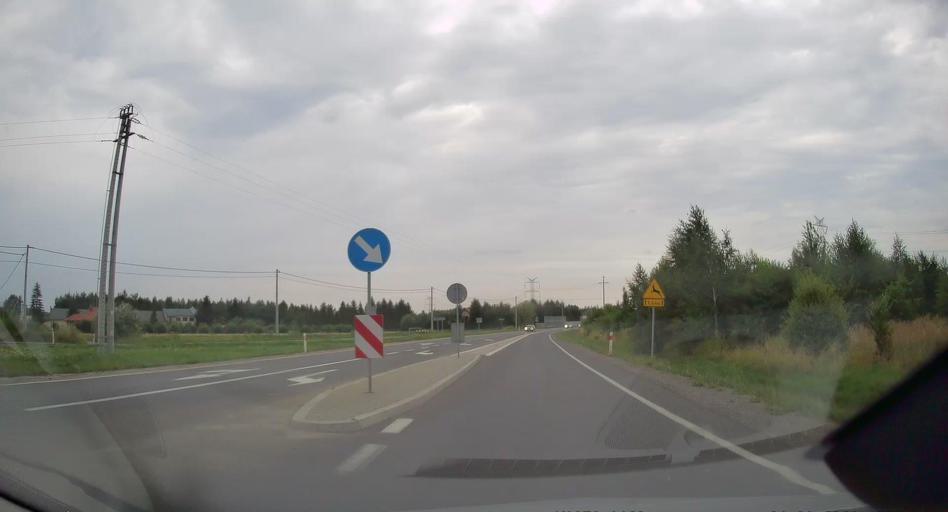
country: PL
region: Lesser Poland Voivodeship
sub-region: Powiat tarnowski
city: Wojnicz
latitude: 49.9810
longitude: 20.8407
